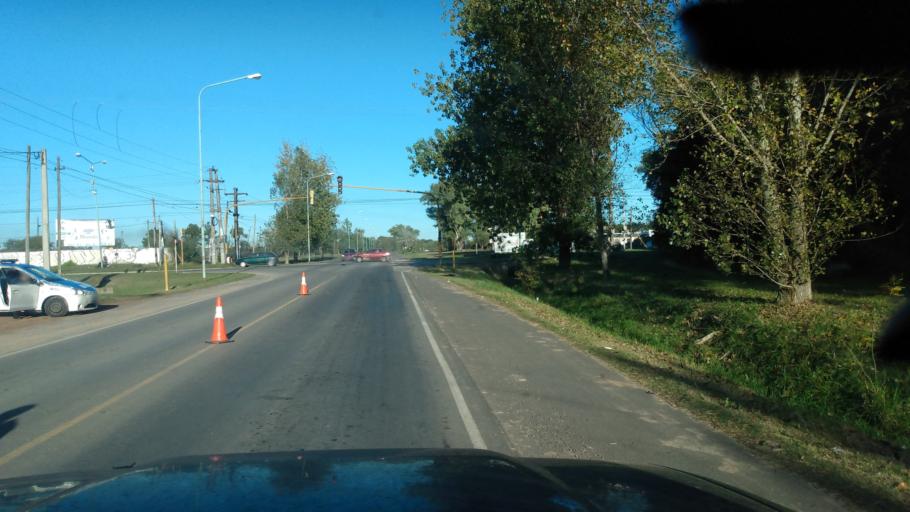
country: AR
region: Buenos Aires
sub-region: Partido de Lujan
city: Lujan
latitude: -34.5619
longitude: -59.1372
